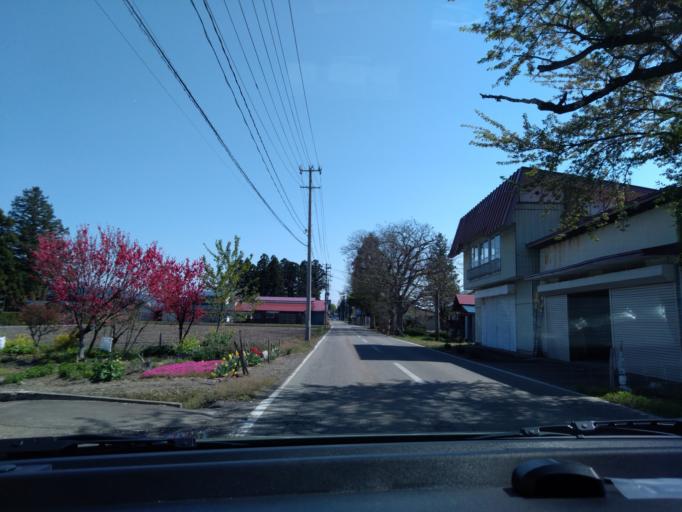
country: JP
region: Akita
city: Kakunodatemachi
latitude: 39.5406
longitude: 140.5853
